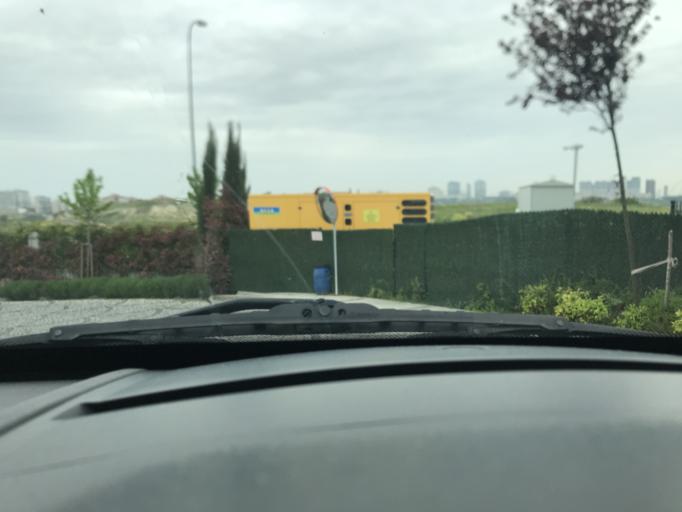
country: TR
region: Istanbul
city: Esenyurt
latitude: 41.0970
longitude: 28.6786
